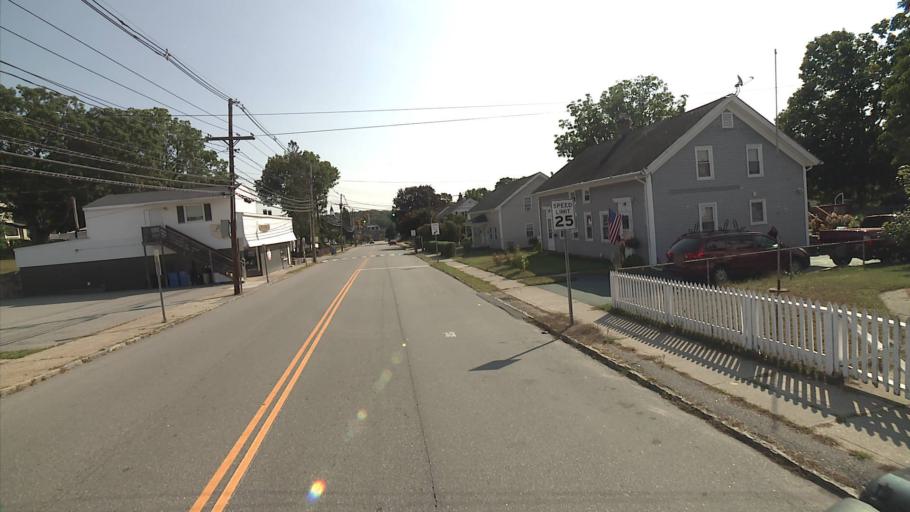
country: US
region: Connecticut
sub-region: New London County
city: Norwich
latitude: 41.5691
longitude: -72.0537
